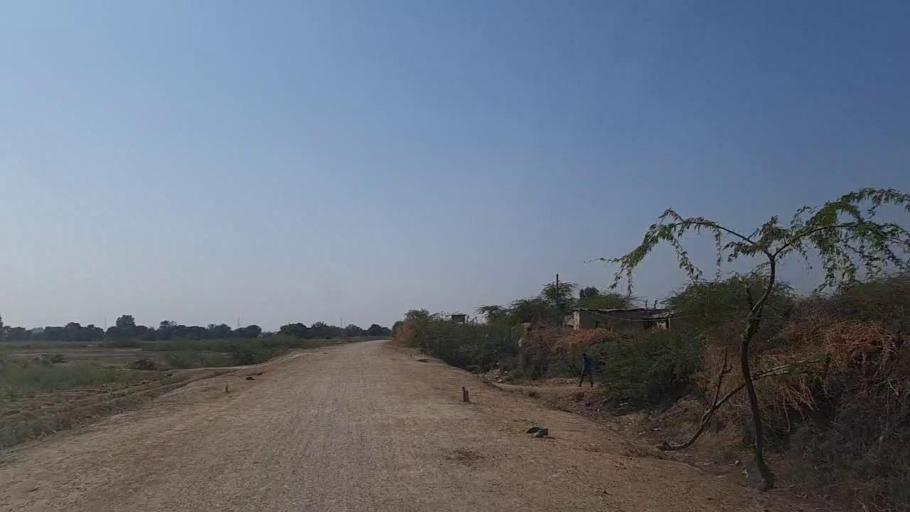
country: PK
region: Sindh
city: Naukot
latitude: 24.8616
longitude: 69.4211
